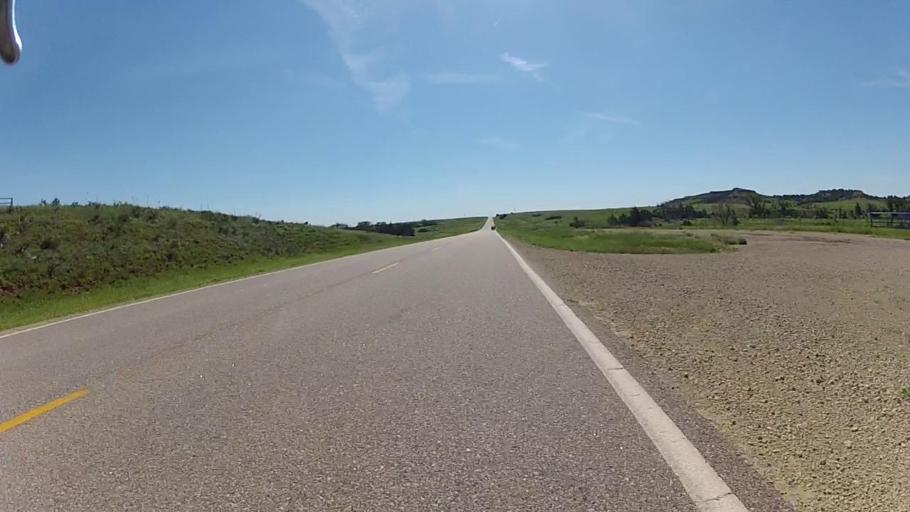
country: US
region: Kansas
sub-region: Barber County
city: Medicine Lodge
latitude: 37.2755
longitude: -98.7176
